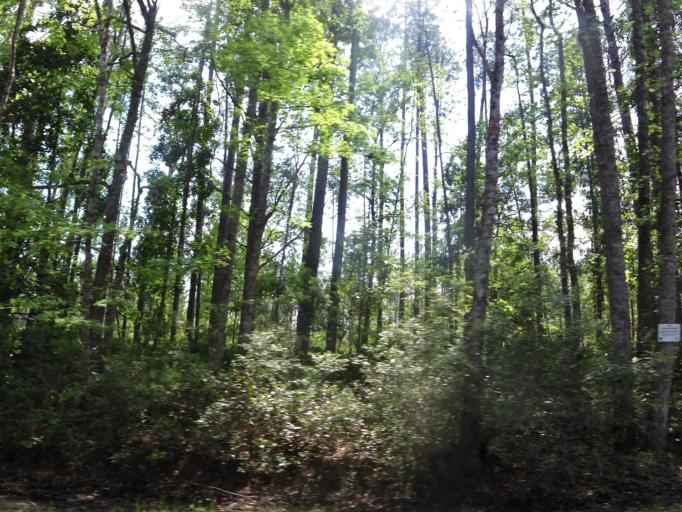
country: US
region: Florida
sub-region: Nassau County
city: Yulee
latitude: 30.5214
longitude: -81.6731
